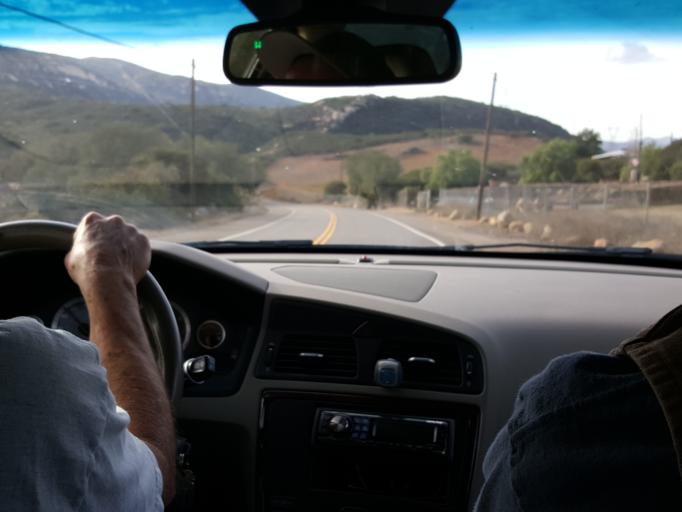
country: US
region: California
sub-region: San Diego County
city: Alpine
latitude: 32.7708
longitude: -116.7001
